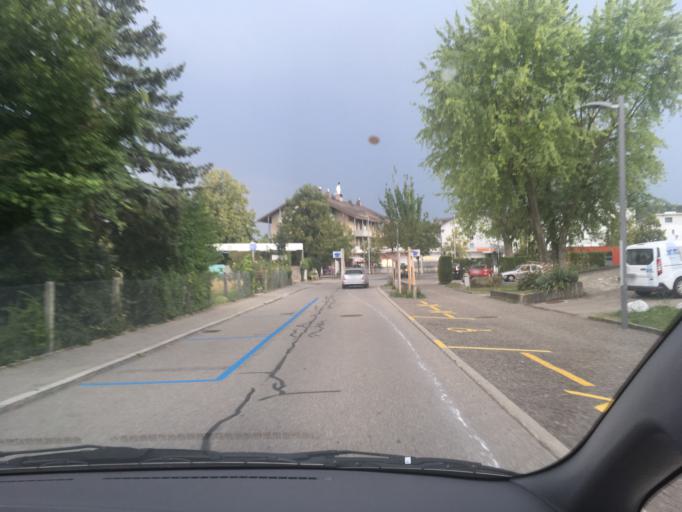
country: CH
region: Bern
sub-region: Bern-Mittelland District
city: Bern
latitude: 46.9765
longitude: 7.4369
